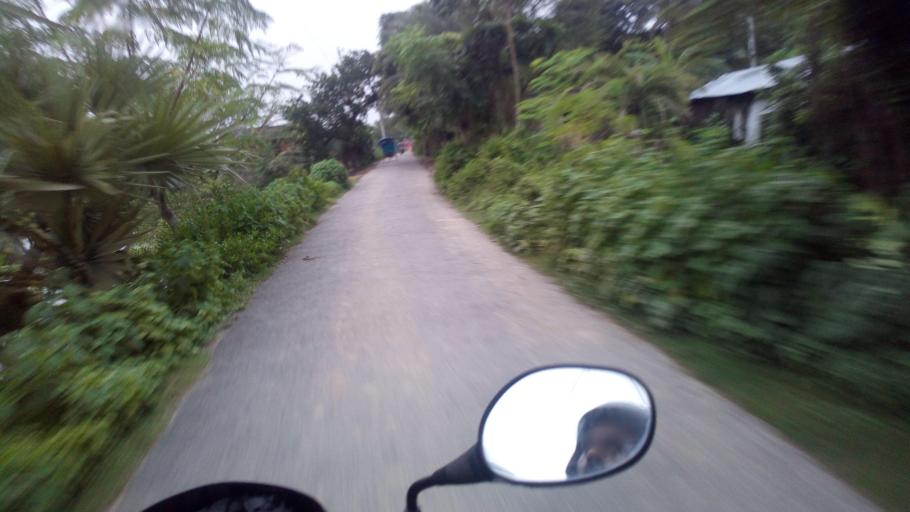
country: BD
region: Khulna
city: Phultala
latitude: 22.7745
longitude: 89.4072
